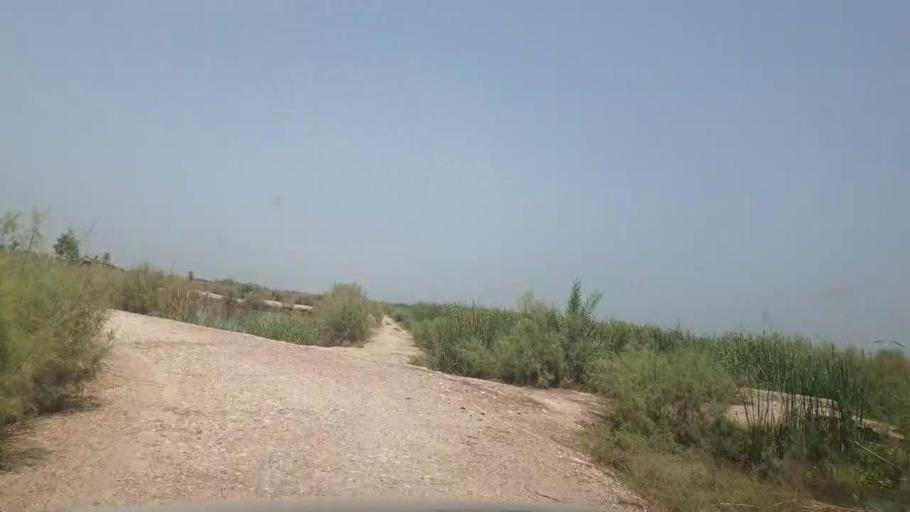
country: PK
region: Sindh
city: Lakhi
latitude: 27.8432
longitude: 68.6275
